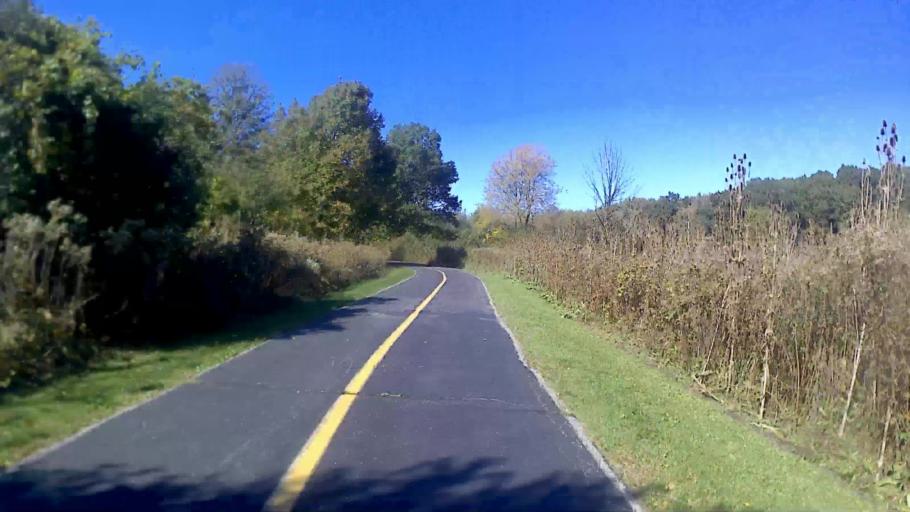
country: US
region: Illinois
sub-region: Cook County
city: Rolling Meadows
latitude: 42.0338
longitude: -88.0221
